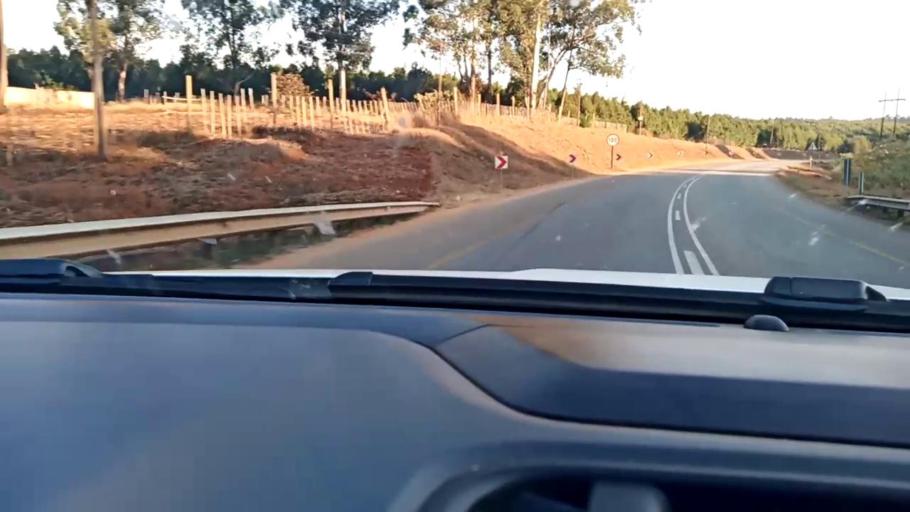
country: ZA
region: Limpopo
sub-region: Mopani District Municipality
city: Duiwelskloof
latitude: -23.7102
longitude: 30.1297
